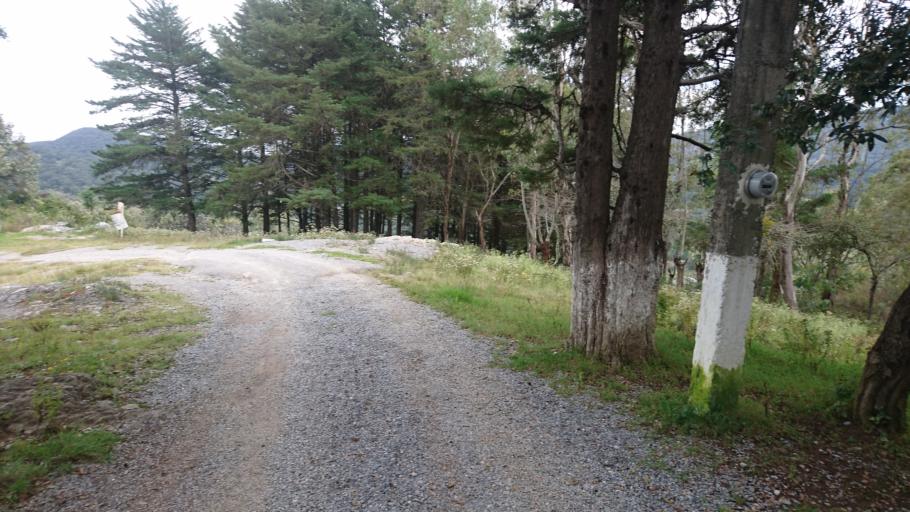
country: MX
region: San Luis Potosi
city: Zaragoza
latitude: 22.0611
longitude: -100.6170
